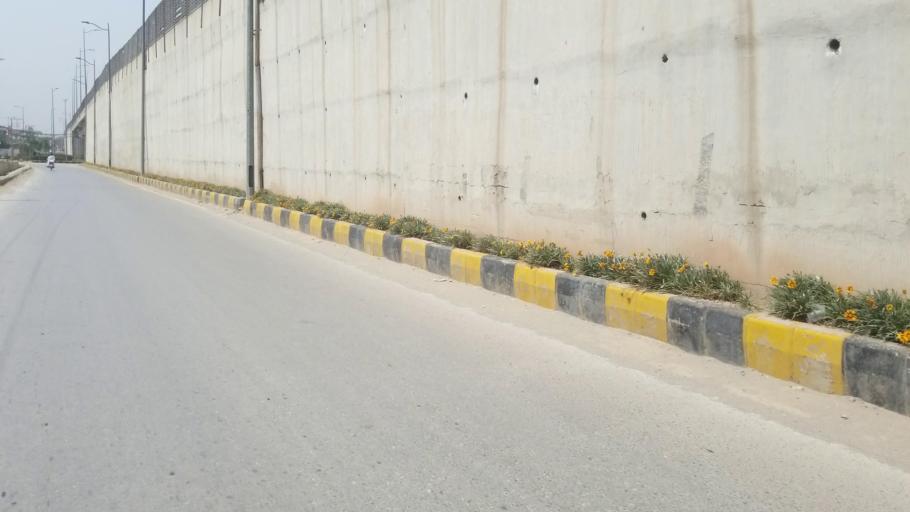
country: PK
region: Khyber Pakhtunkhwa
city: Peshawar
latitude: 34.0320
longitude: 71.5559
